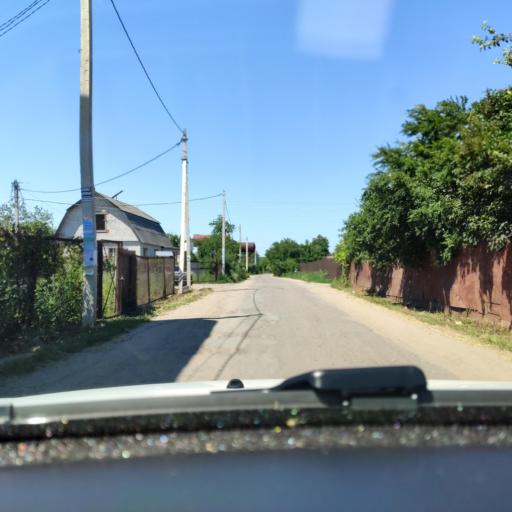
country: RU
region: Voronezj
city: Shilovo
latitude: 51.5871
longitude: 39.1560
